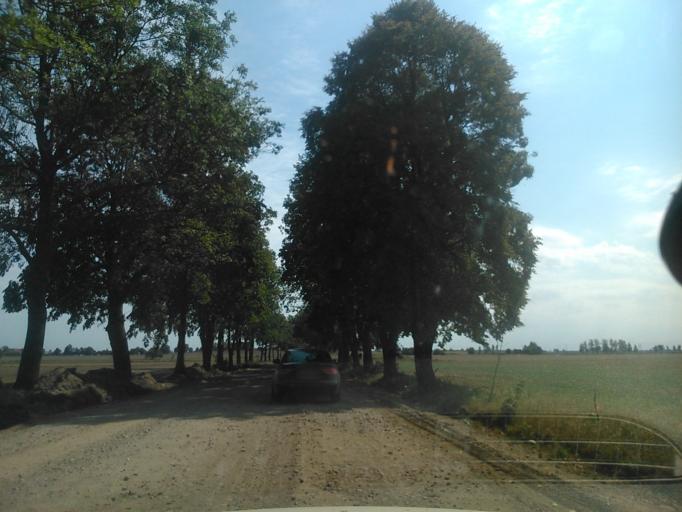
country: PL
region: Warmian-Masurian Voivodeship
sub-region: Powiat dzialdowski
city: Dzialdowo
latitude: 53.2110
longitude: 20.2284
